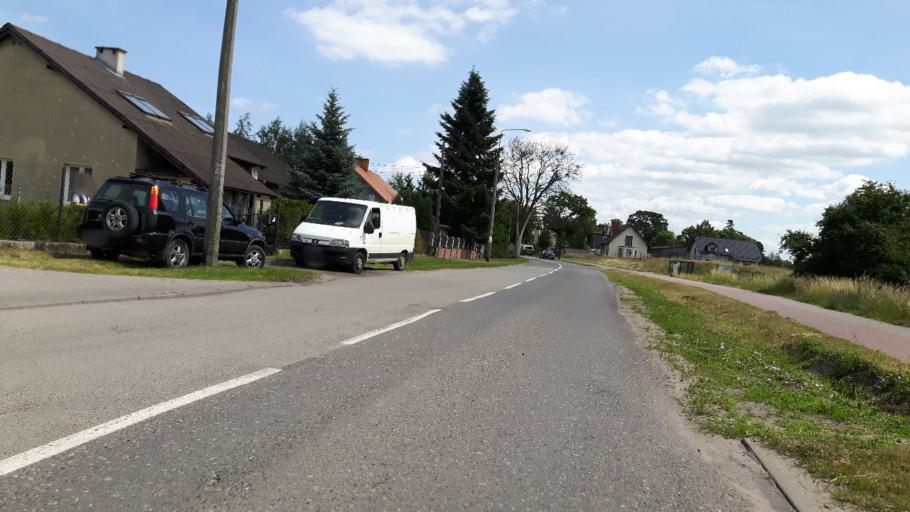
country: PL
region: Pomeranian Voivodeship
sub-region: Powiat gdanski
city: Cedry Wielkie
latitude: 54.3365
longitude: 18.9168
